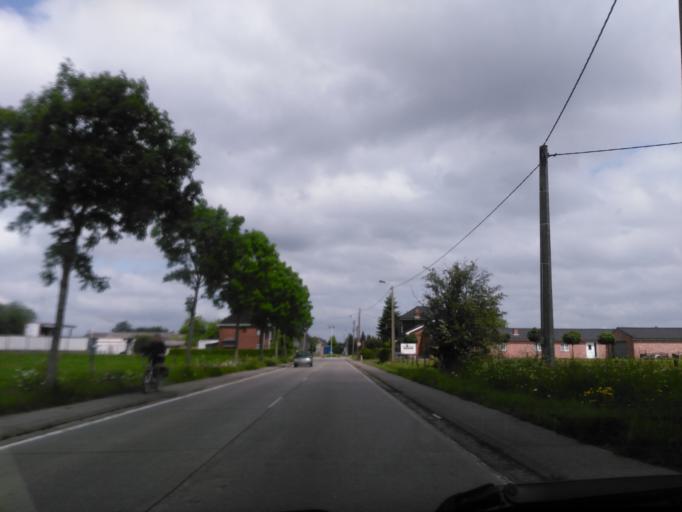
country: BE
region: Flanders
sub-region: Provincie Oost-Vlaanderen
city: Beveren
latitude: 51.1988
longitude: 4.2669
